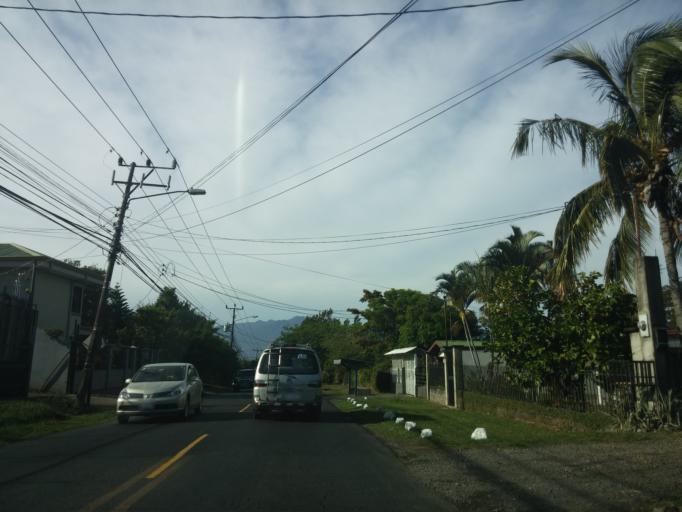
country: CR
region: Heredia
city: Llorente
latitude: 10.0130
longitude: -84.1523
